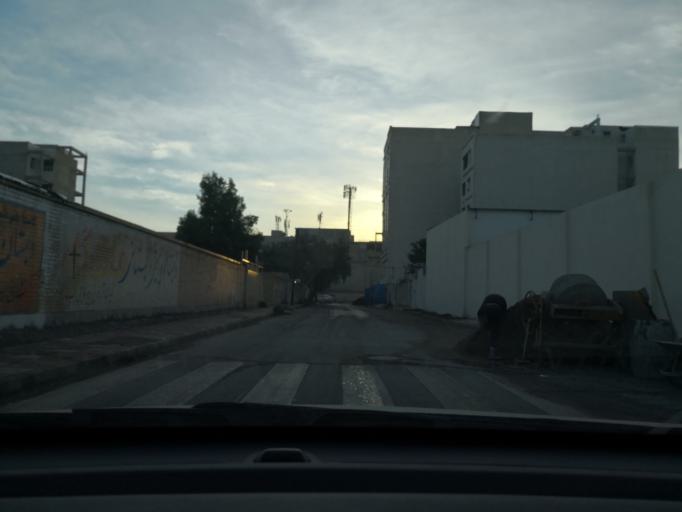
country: IR
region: Khuzestan
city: Ahvaz
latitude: 31.3519
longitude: 48.6790
